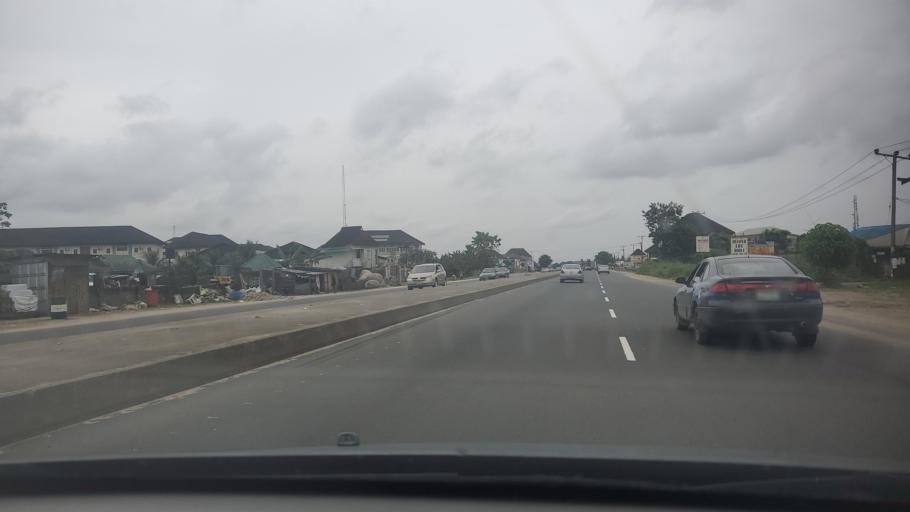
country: NG
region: Rivers
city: Emuoha
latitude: 4.8739
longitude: 6.9586
